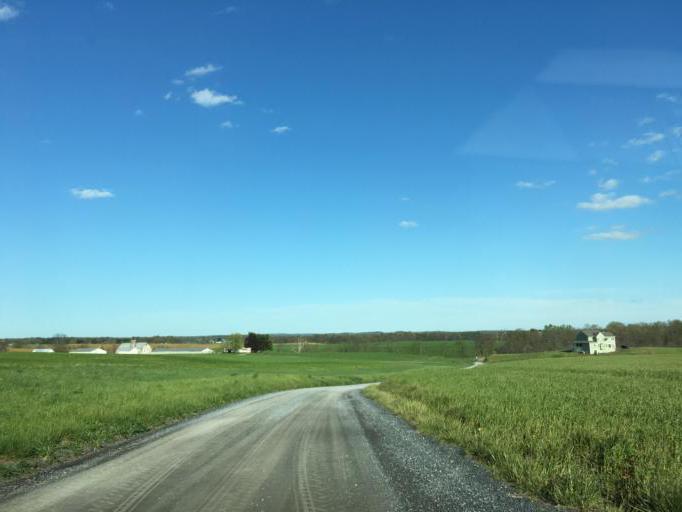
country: US
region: Maryland
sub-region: Frederick County
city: Woodsboro
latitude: 39.6183
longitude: -77.2672
